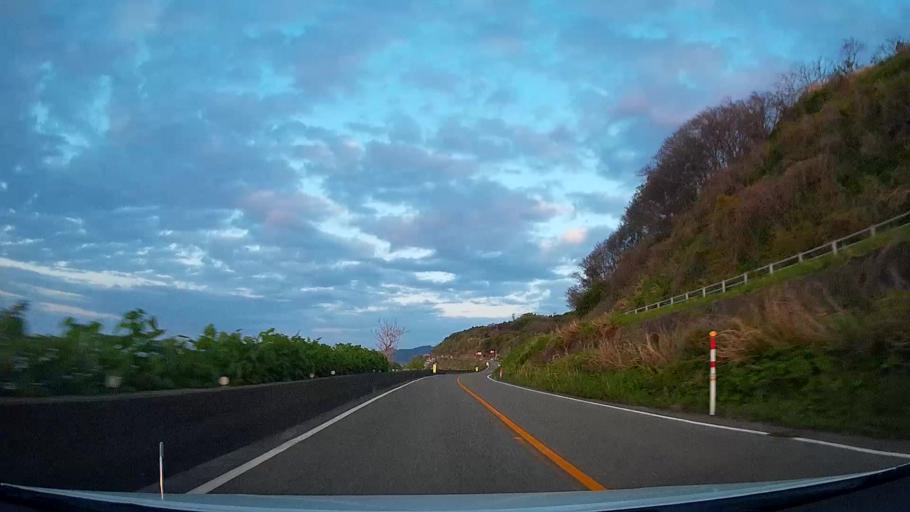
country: JP
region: Niigata
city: Joetsu
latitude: 37.1720
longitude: 138.1115
